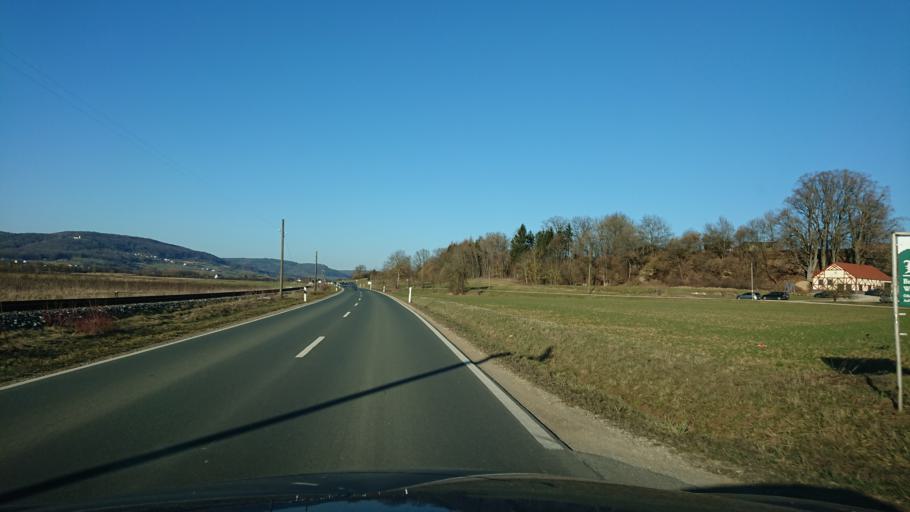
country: DE
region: Bavaria
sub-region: Upper Franconia
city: Wiesenthau
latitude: 49.7214
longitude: 11.1340
